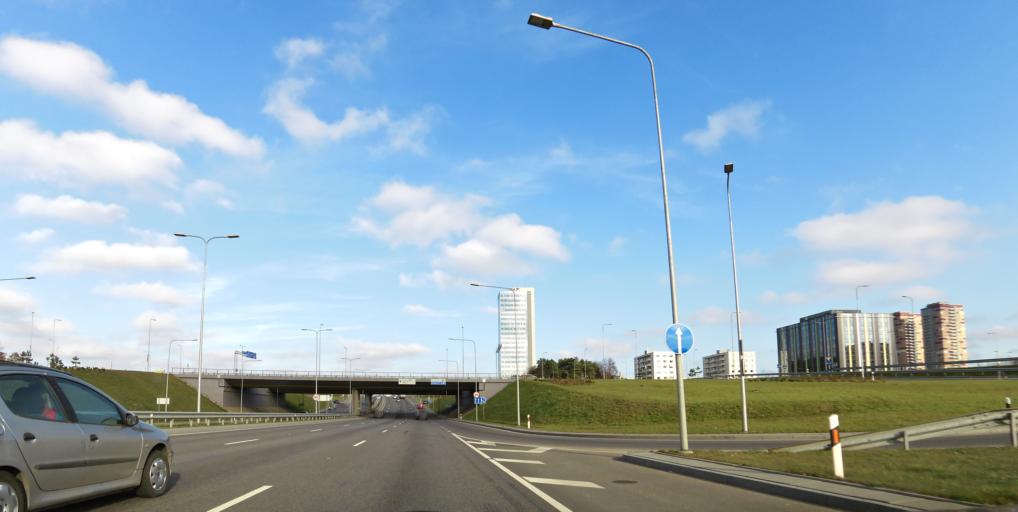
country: LT
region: Vilnius County
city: Justiniskes
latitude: 54.6993
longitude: 25.2079
